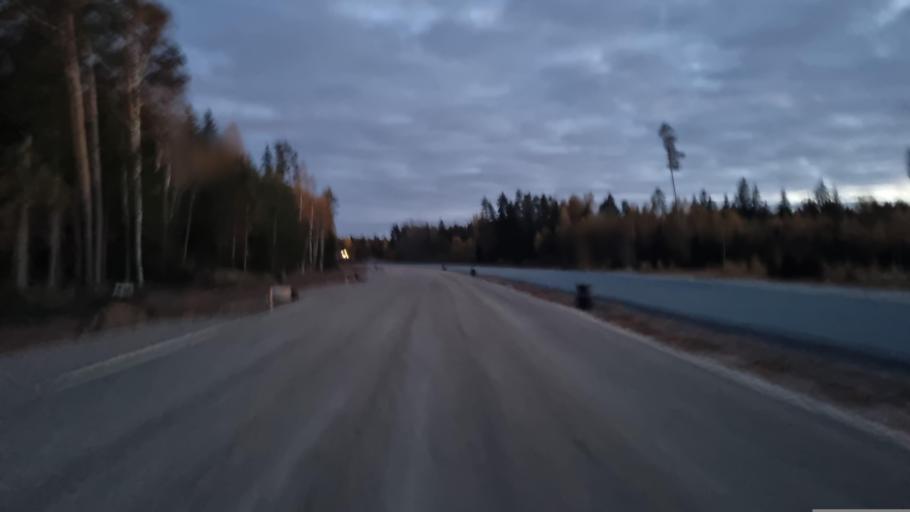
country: LV
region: Kekava
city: Balozi
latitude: 56.8323
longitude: 24.1572
